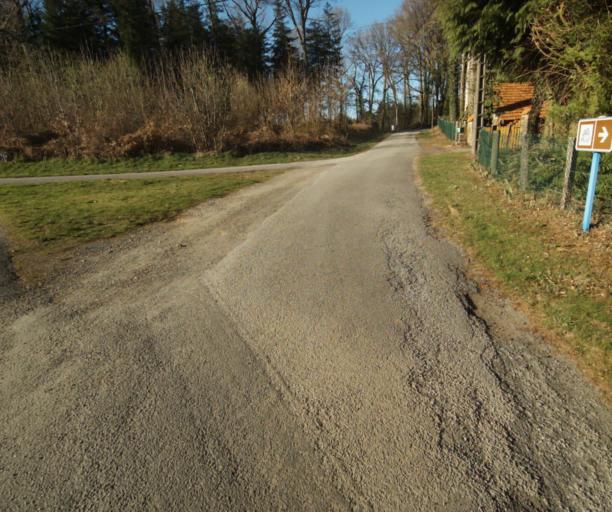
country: FR
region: Limousin
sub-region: Departement de la Correze
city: Seilhac
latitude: 45.3843
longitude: 1.6994
